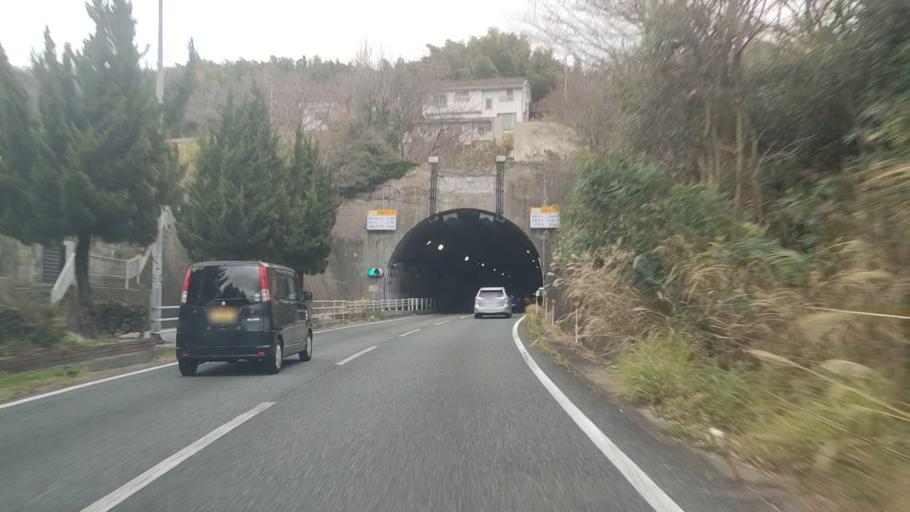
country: JP
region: Yamaguchi
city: Shimonoseki
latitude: 33.9701
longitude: 130.9427
